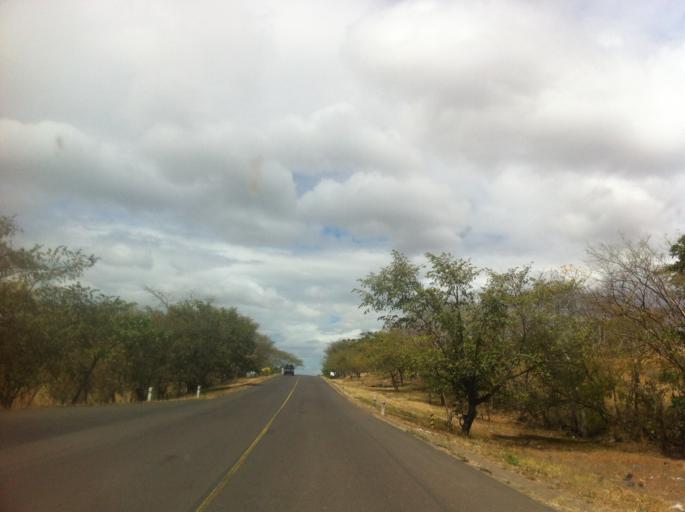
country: NI
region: Chontales
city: Juigalpa
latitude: 12.0450
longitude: -85.2819
